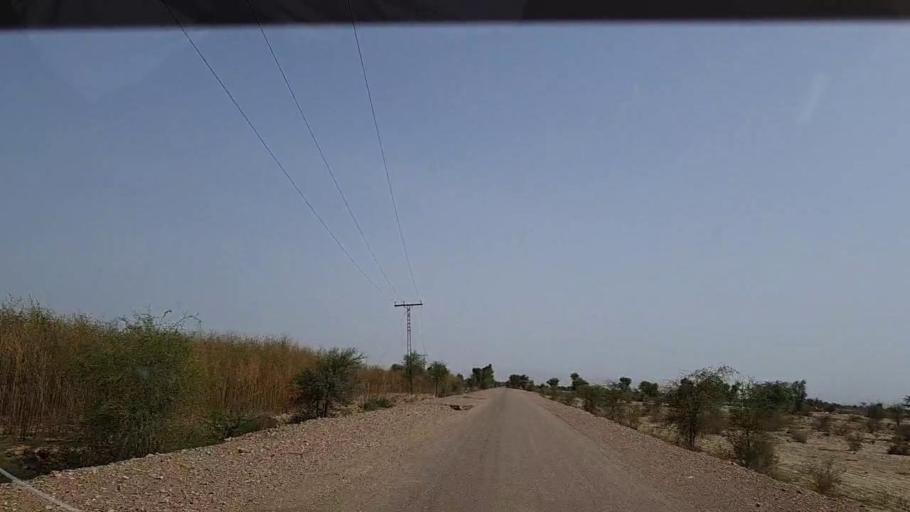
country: PK
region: Sindh
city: Johi
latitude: 26.6573
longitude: 67.5057
